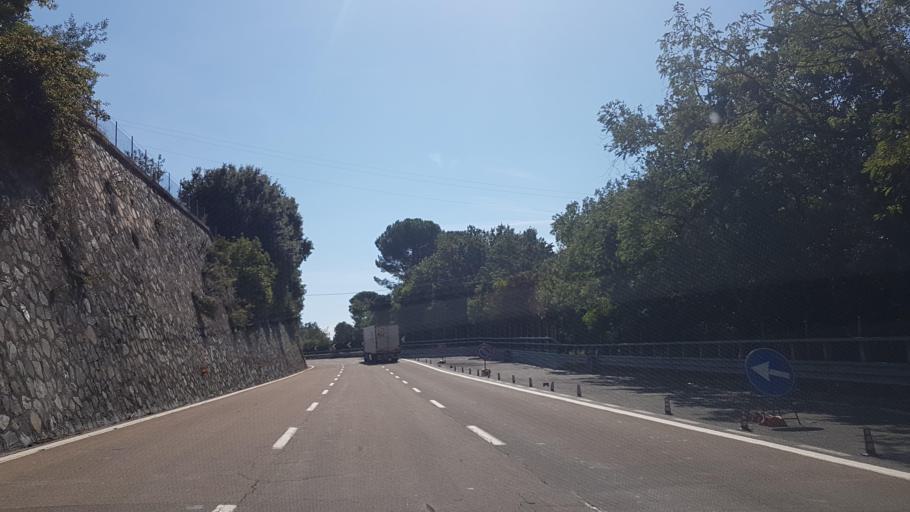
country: IT
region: Liguria
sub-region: Provincia di Genova
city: Arenzano
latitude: 44.4190
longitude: 8.7168
